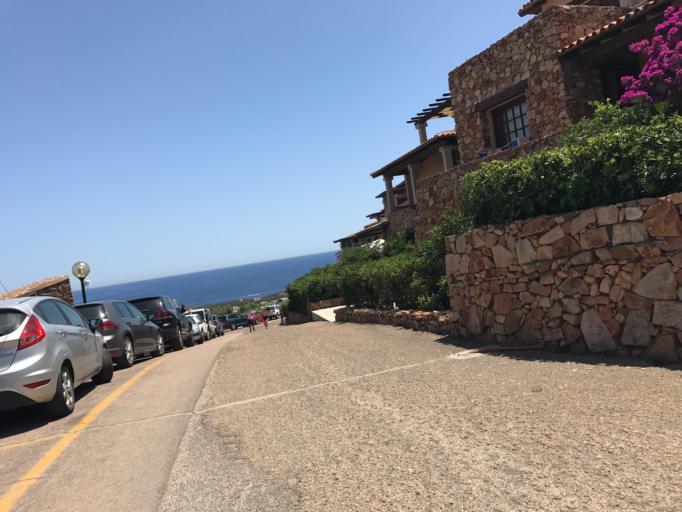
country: IT
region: Sardinia
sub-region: Provincia di Olbia-Tempio
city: San Teodoro
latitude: 40.8400
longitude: 9.7157
